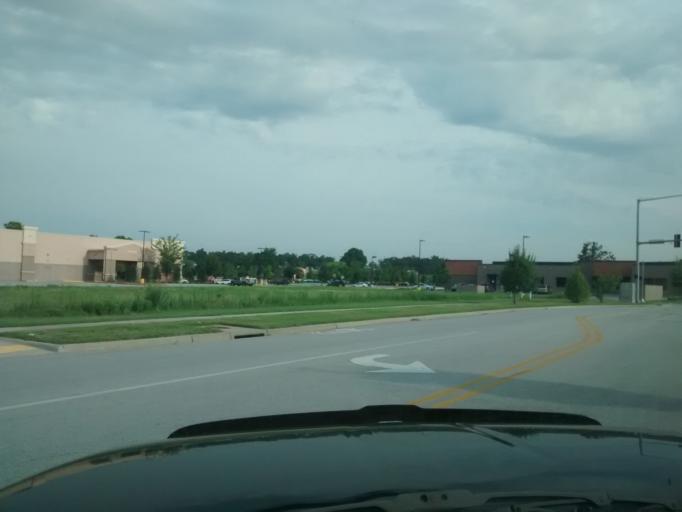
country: US
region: Arkansas
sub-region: Washington County
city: Farmington
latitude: 36.0757
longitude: -94.2088
